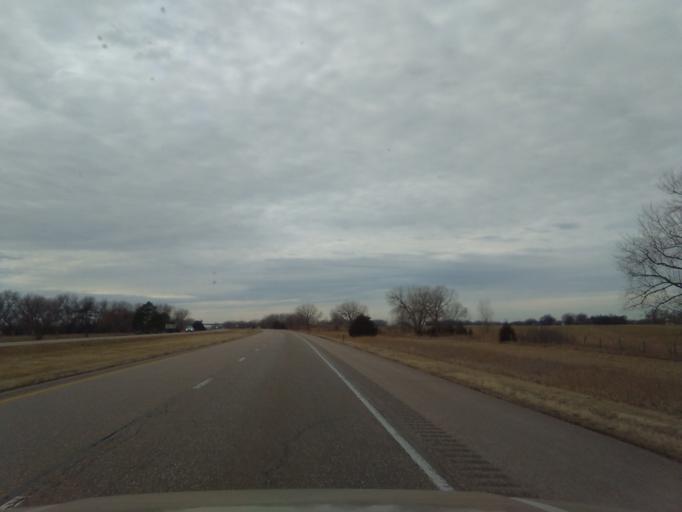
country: US
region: Nebraska
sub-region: Hall County
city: Wood River
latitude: 40.7601
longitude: -98.5978
